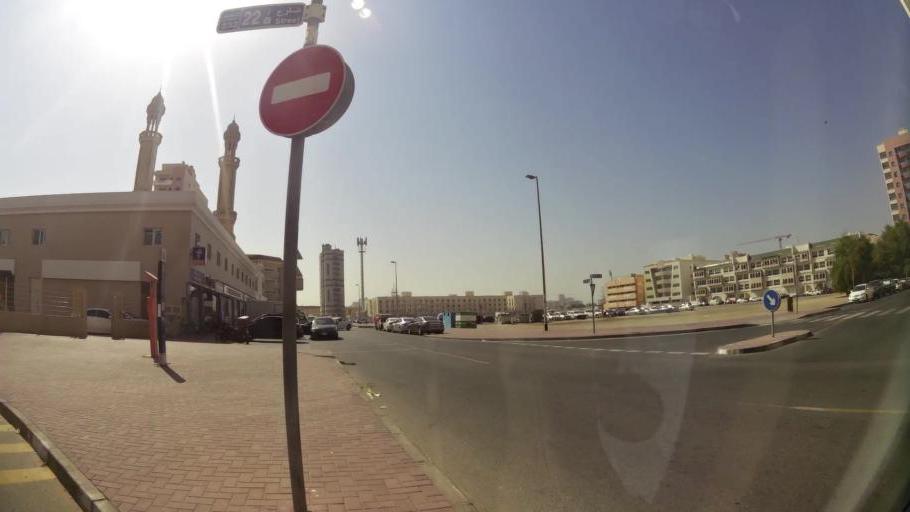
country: AE
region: Ash Shariqah
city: Sharjah
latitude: 25.2746
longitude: 55.3729
